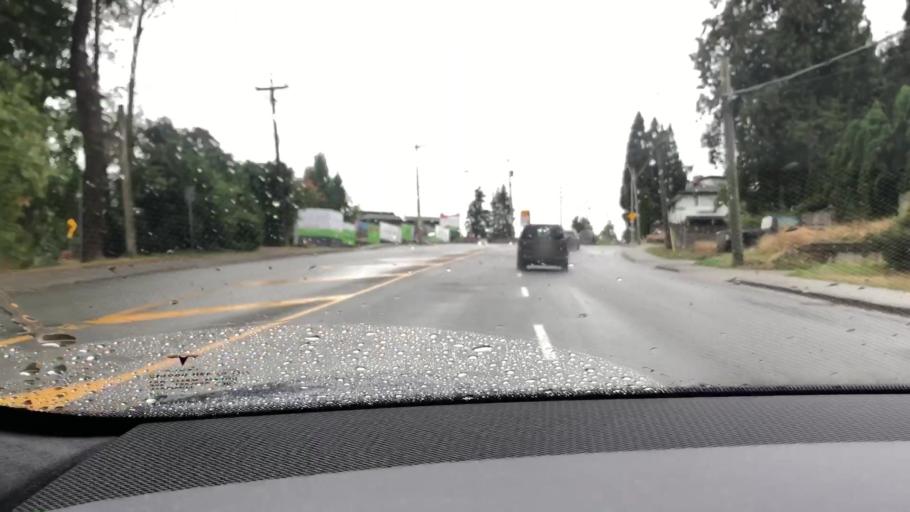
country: CA
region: British Columbia
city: Port Moody
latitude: 49.2731
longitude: -122.8760
